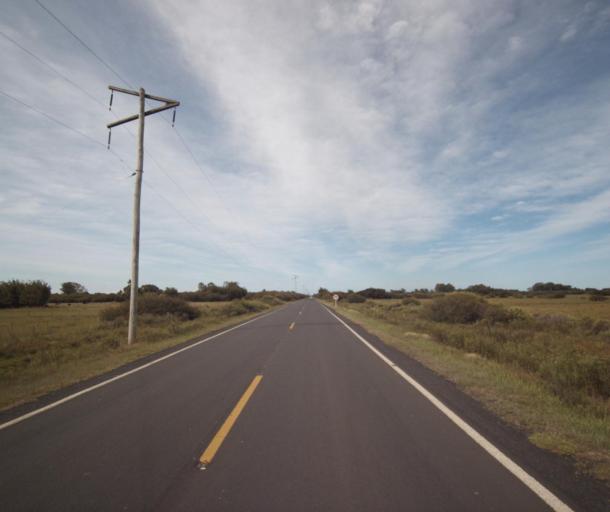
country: BR
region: Rio Grande do Sul
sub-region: Rio Grande
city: Rio Grande
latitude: -31.9202
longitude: -51.9477
